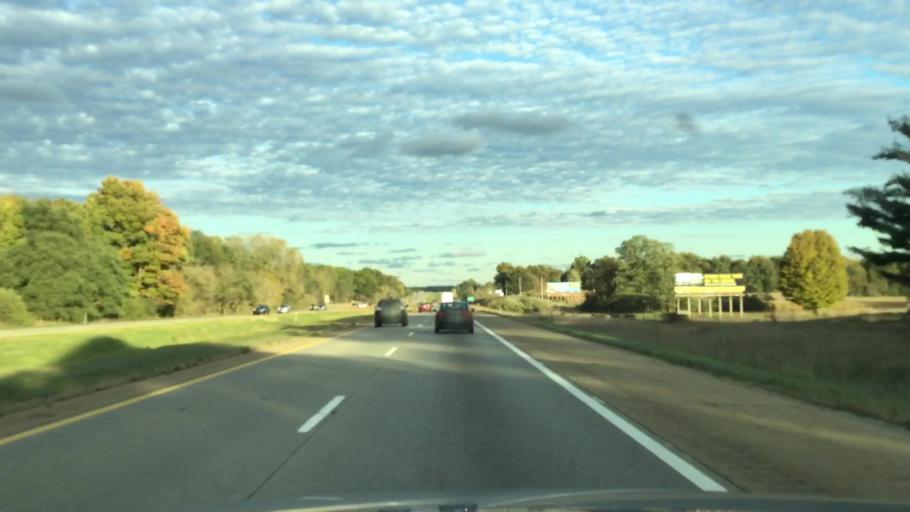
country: US
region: Michigan
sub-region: Jackson County
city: Concord
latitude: 42.2620
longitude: -84.6661
